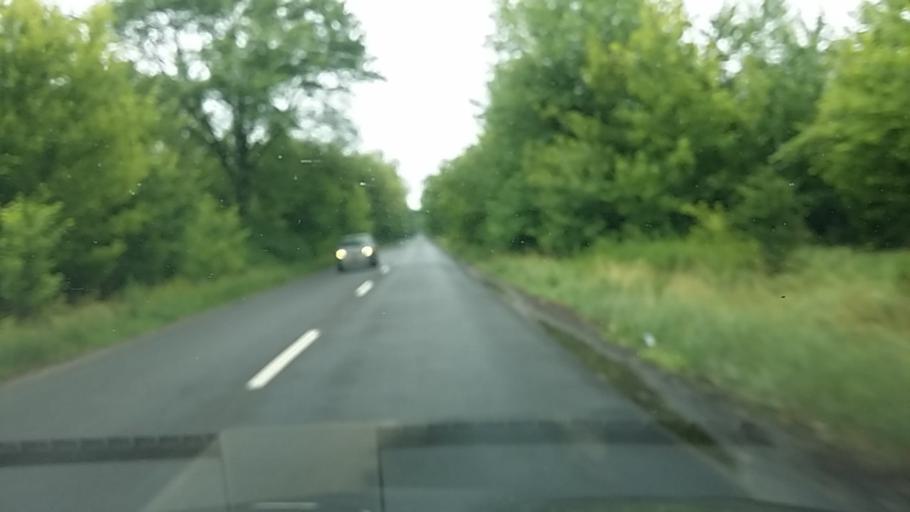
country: SK
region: Nitriansky
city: Zeliezovce
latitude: 47.9630
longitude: 18.7822
